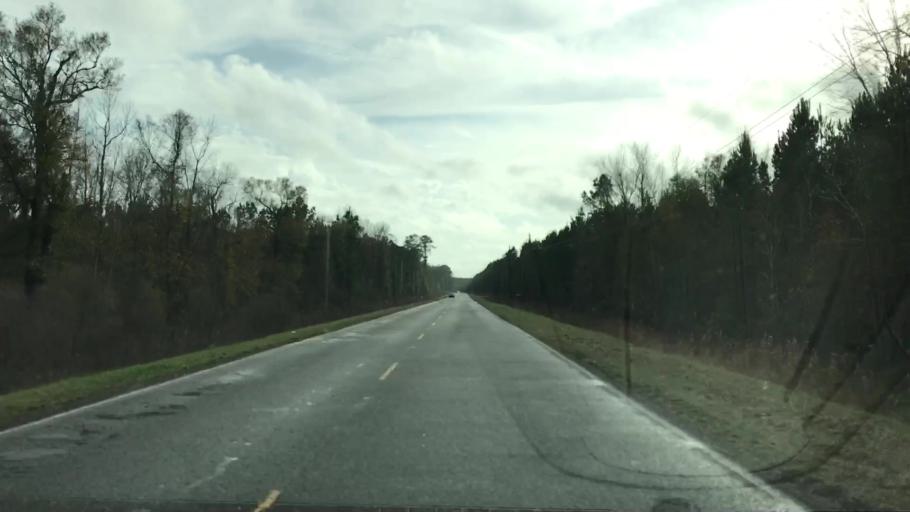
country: US
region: South Carolina
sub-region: Williamsburg County
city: Andrews
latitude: 33.4317
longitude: -79.5936
